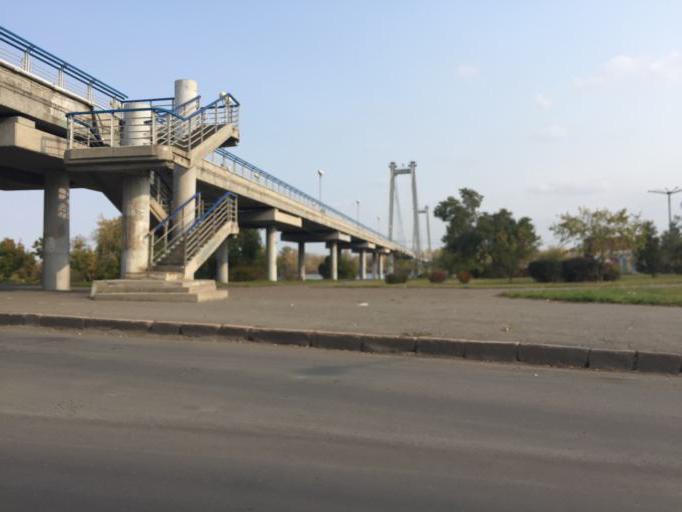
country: RU
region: Krasnoyarskiy
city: Krasnoyarsk
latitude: 56.0133
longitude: 92.8967
